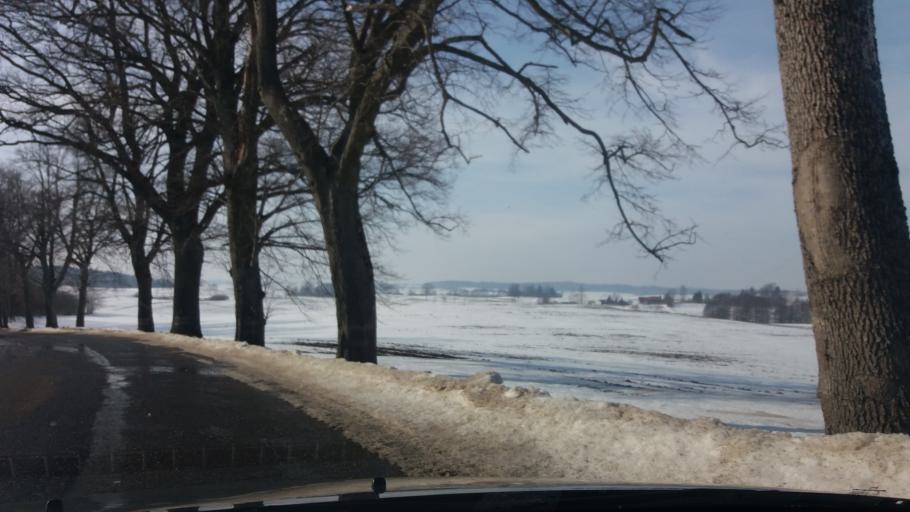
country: PL
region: Warmian-Masurian Voivodeship
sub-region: Powiat bartoszycki
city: Bisztynek
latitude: 54.1112
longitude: 20.8395
